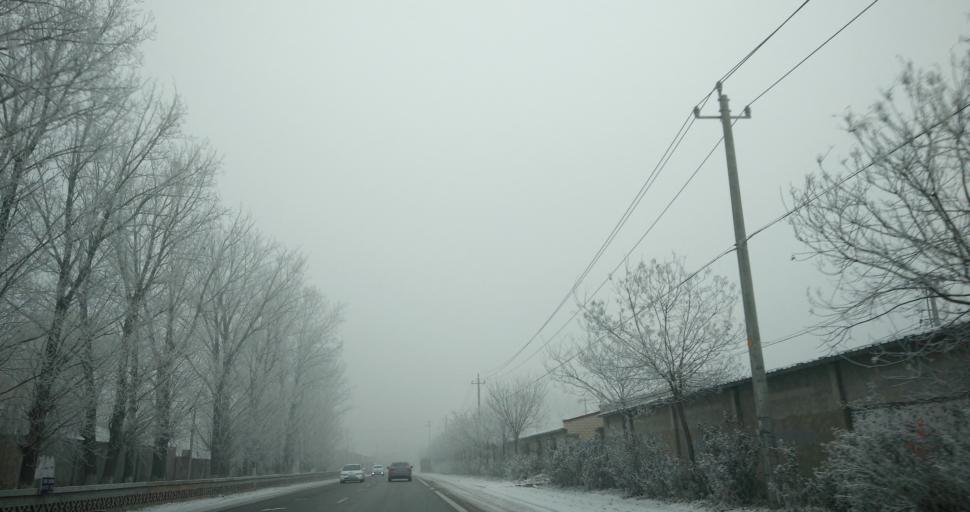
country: CN
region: Beijing
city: Yinghai
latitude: 39.7037
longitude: 116.4162
